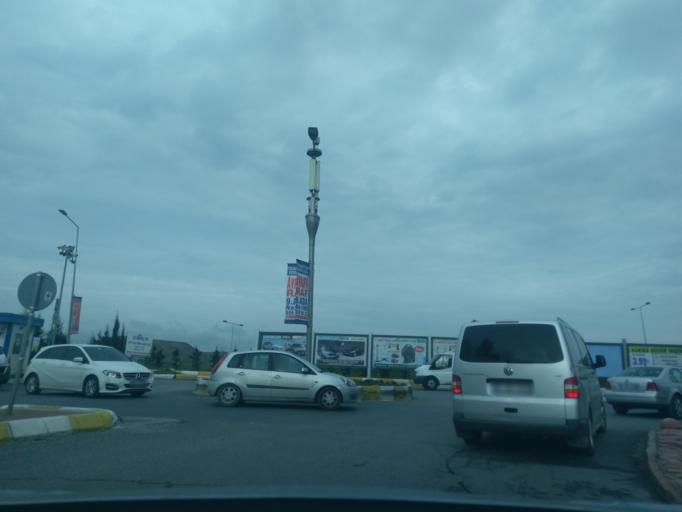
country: TR
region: Istanbul
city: Mahmutbey
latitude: 41.0705
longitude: 28.8198
